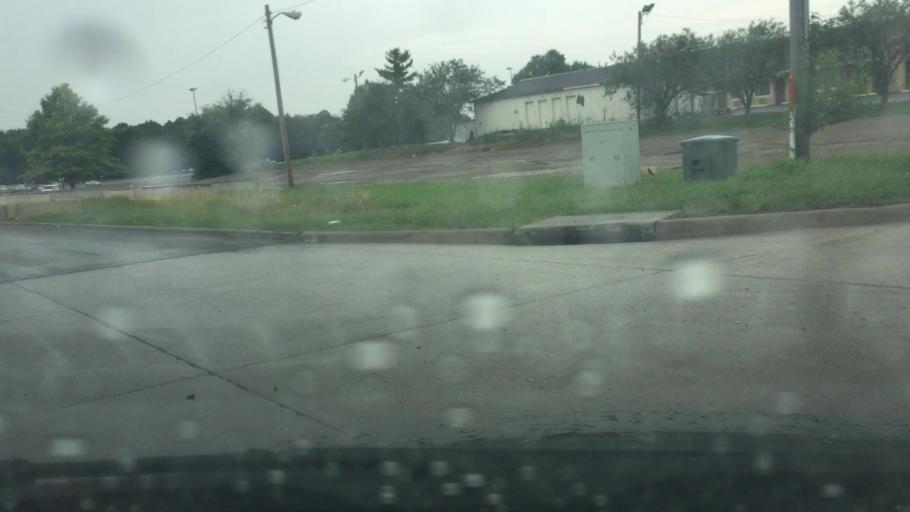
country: US
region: Illinois
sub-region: Williamson County
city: Marion
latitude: 37.7396
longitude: -88.9654
